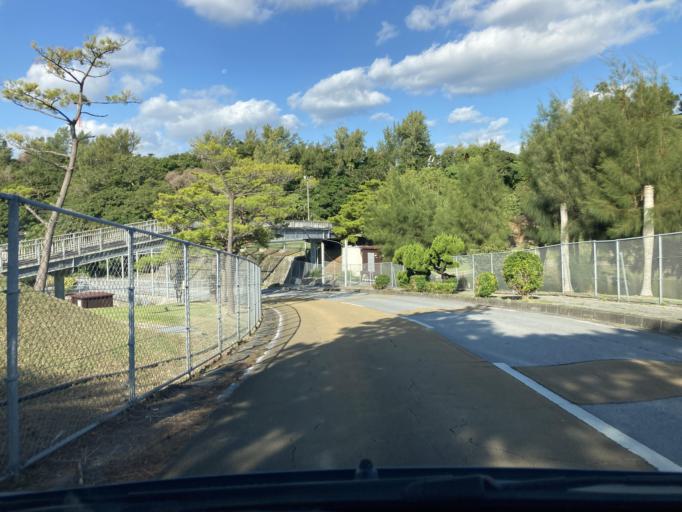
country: JP
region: Okinawa
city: Ginowan
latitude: 26.2159
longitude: 127.7461
